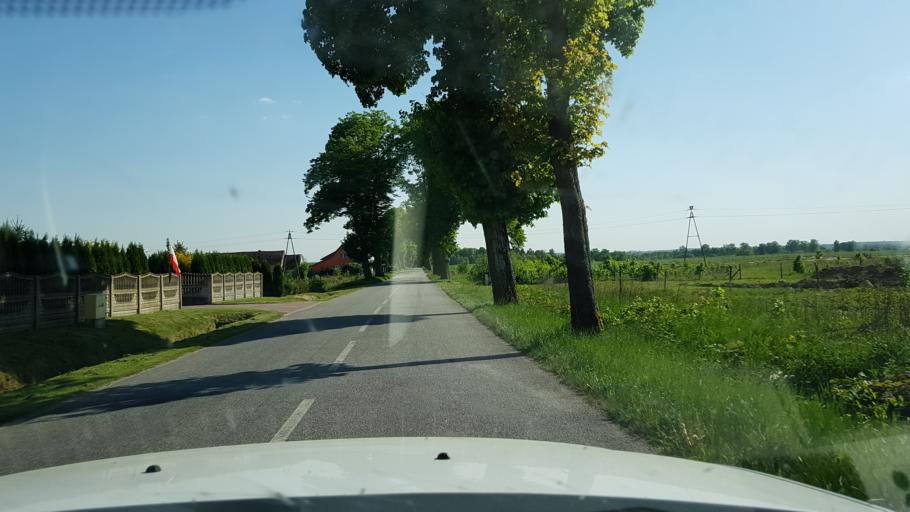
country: PL
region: West Pomeranian Voivodeship
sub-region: Powiat lobeski
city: Resko
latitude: 53.7870
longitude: 15.4108
